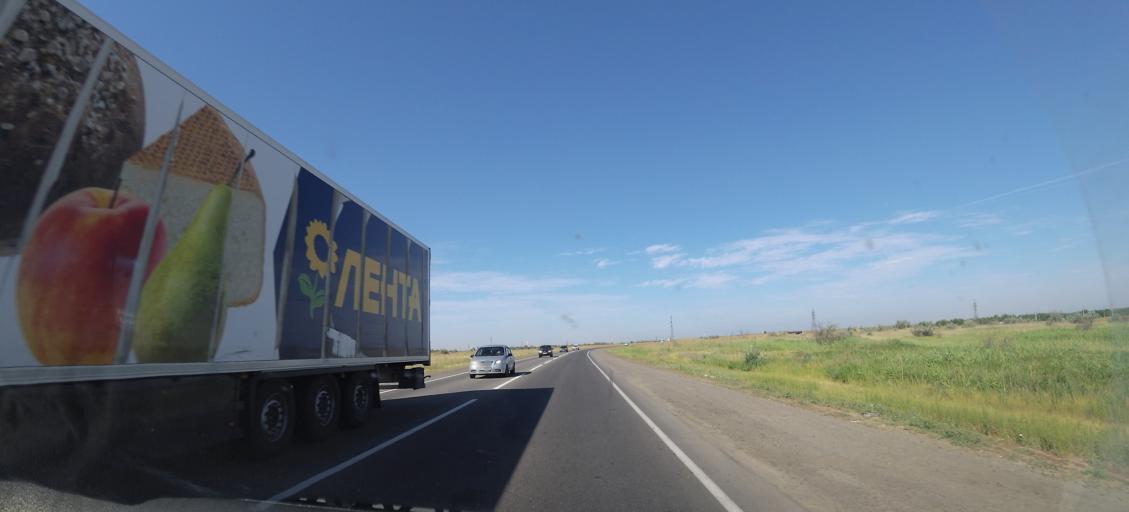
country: RU
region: Volgograd
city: Oktyabr'skiy
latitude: 48.6753
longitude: 43.8870
